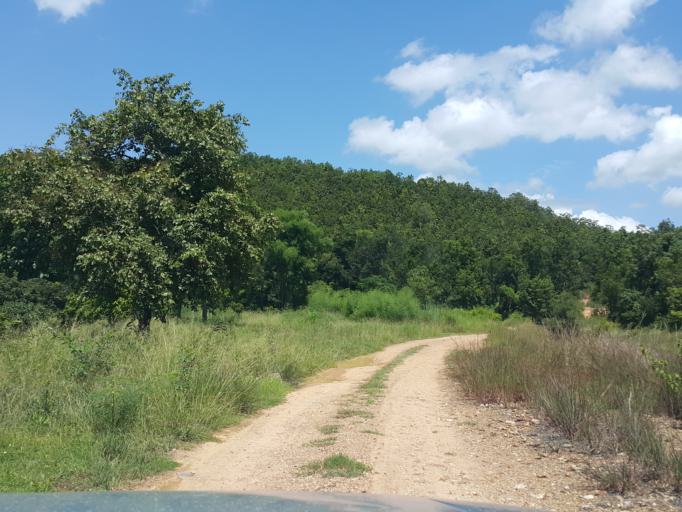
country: TH
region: Chiang Mai
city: San Kamphaeng
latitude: 18.7171
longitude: 99.1846
